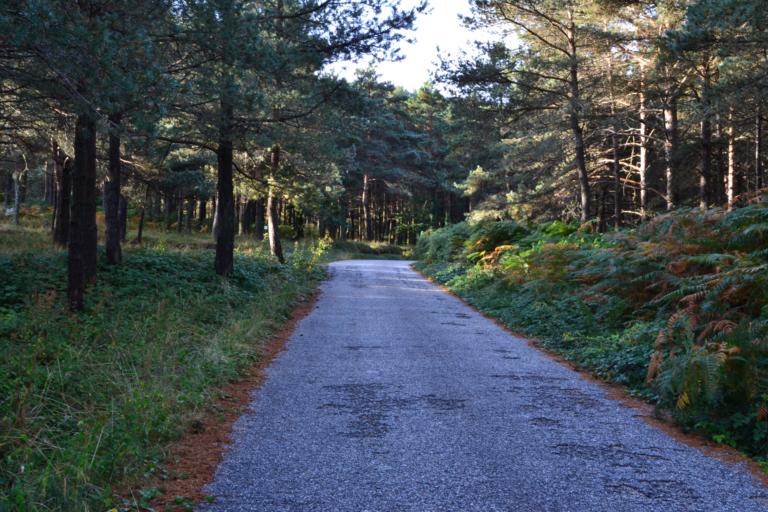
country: PT
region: Vila Real
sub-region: Mesao Frio
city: Mesao Frio
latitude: 41.2786
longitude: -7.9147
